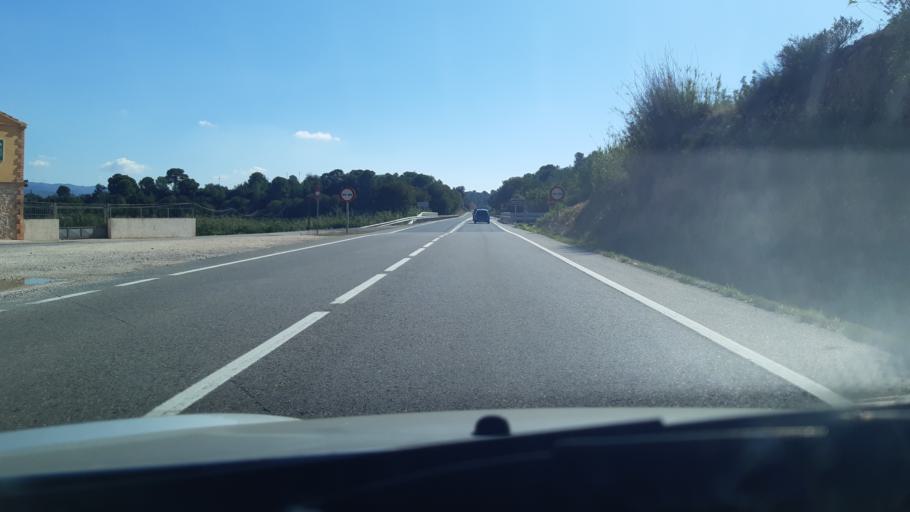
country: ES
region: Catalonia
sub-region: Provincia de Tarragona
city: Tivenys
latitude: 40.8921
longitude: 0.4898
